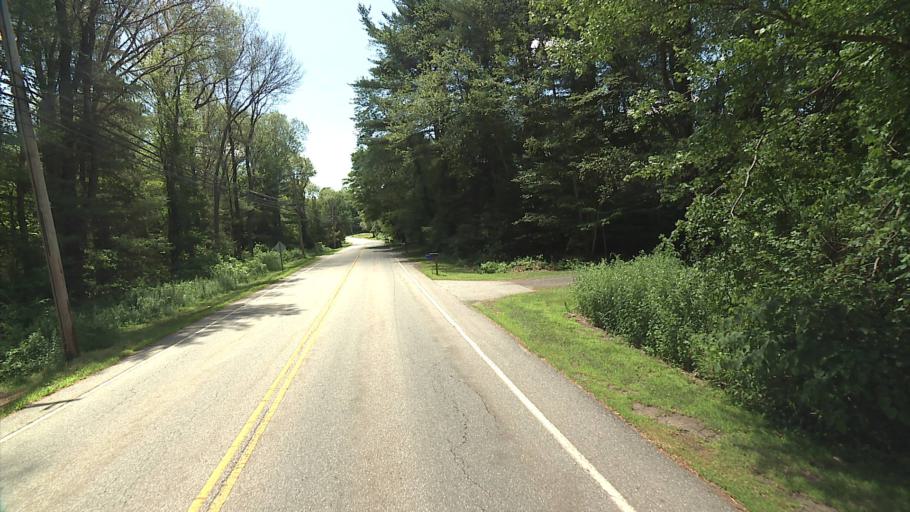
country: US
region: Connecticut
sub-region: Middlesex County
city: East Hampton
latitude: 41.5520
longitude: -72.5094
